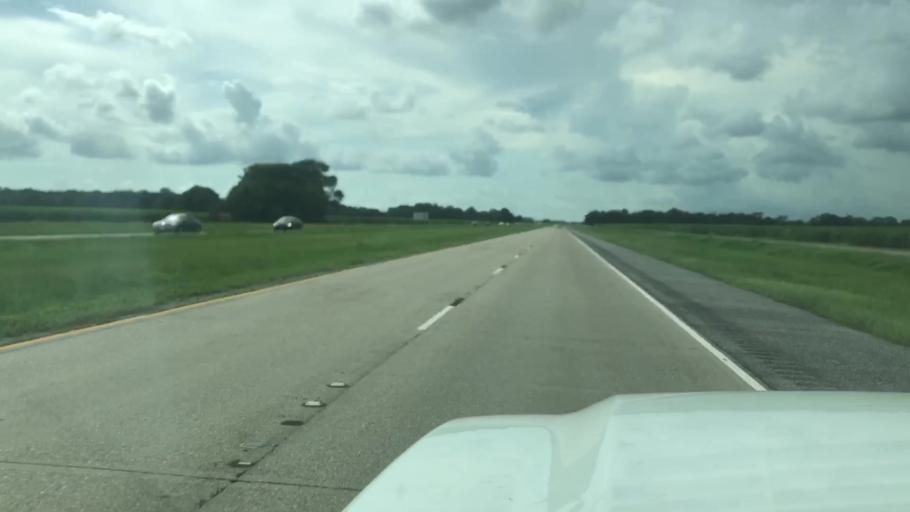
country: US
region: Louisiana
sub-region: Saint Mary Parish
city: Franklin
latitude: 29.7602
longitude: -91.4775
